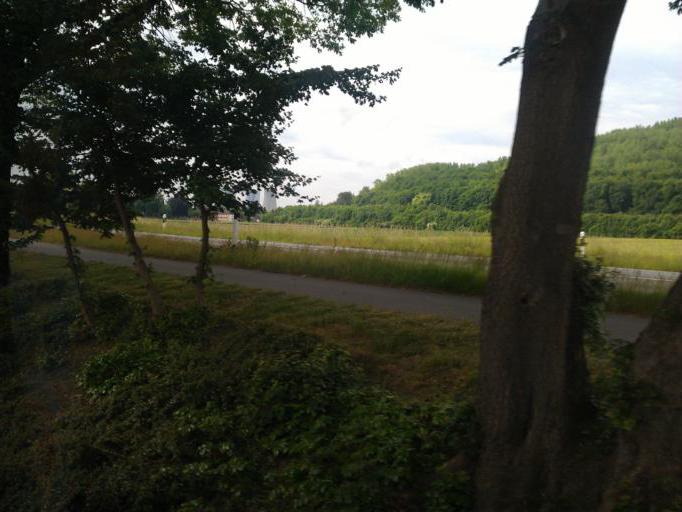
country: DE
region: North Rhine-Westphalia
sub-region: Regierungsbezirk Dusseldorf
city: Grevenbroich
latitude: 51.0741
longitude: 6.6233
